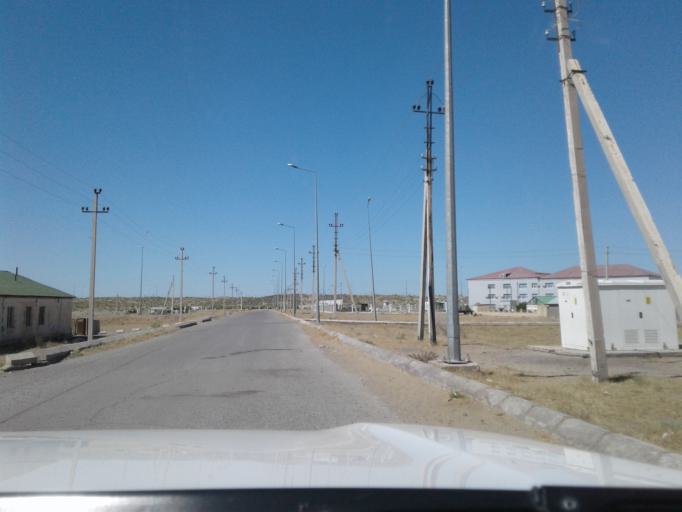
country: TM
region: Mary
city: Bayramaly
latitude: 38.0876
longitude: 62.7947
